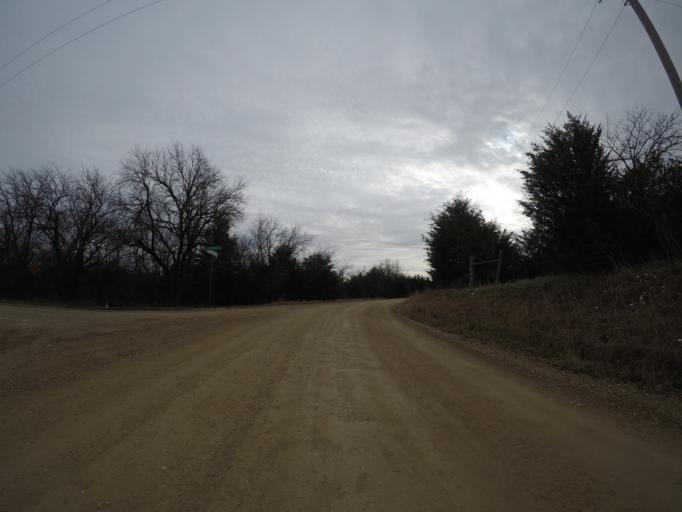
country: US
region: Kansas
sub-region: Riley County
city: Ogden
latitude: 39.1750
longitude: -96.6781
